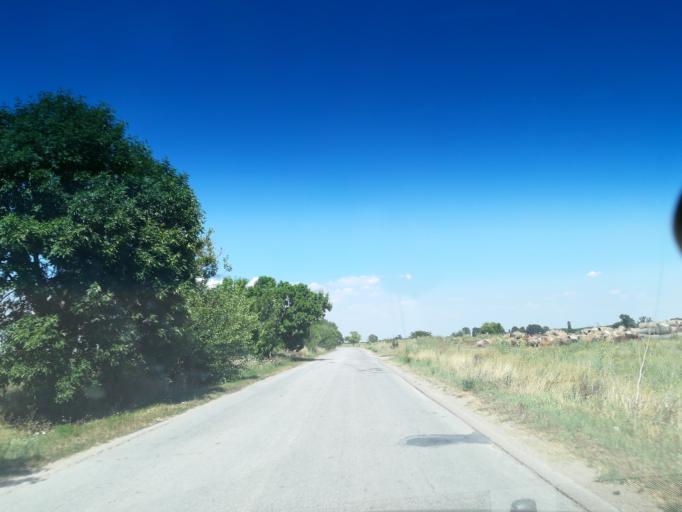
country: BG
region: Plovdiv
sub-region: Obshtina Sadovo
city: Sadovo
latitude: 42.0347
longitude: 25.1216
